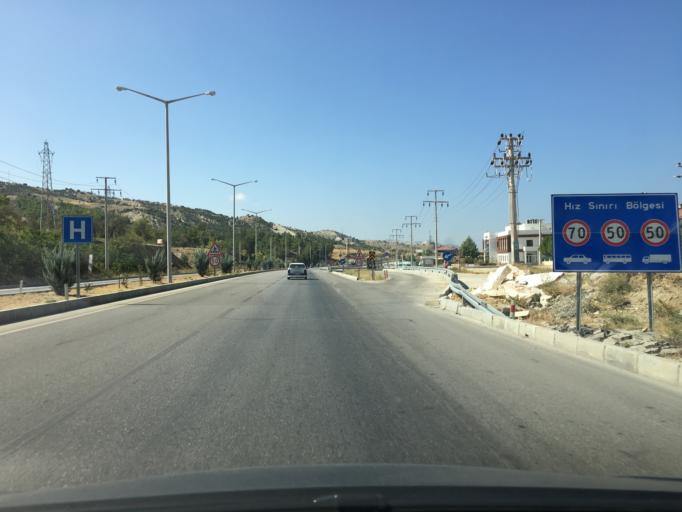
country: TR
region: Burdur
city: Burdur
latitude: 37.7538
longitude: 30.3344
